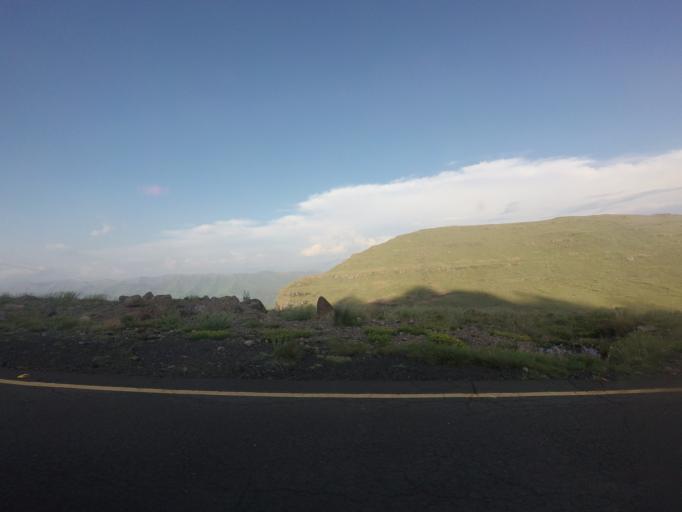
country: LS
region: Butha-Buthe
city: Butha-Buthe
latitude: -29.0724
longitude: 28.4252
